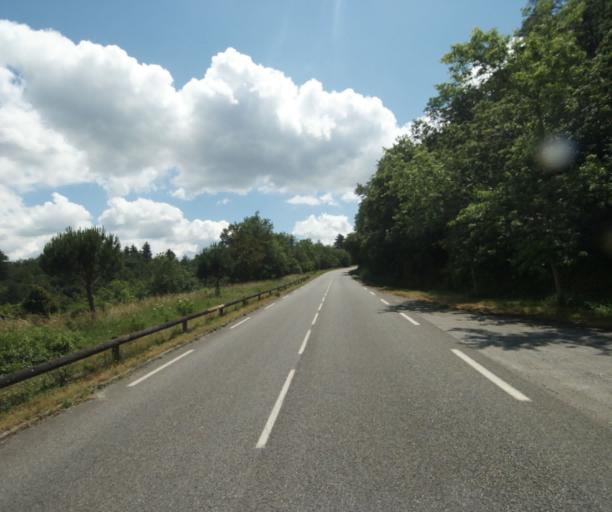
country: FR
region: Midi-Pyrenees
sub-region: Departement de la Haute-Garonne
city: Revel
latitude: 43.4442
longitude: 2.0195
